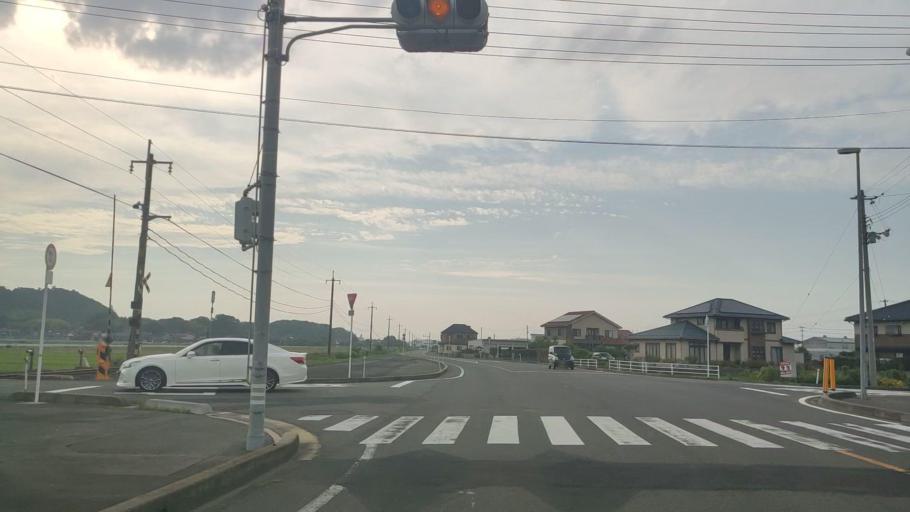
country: JP
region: Tottori
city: Kurayoshi
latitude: 35.4762
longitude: 133.8206
